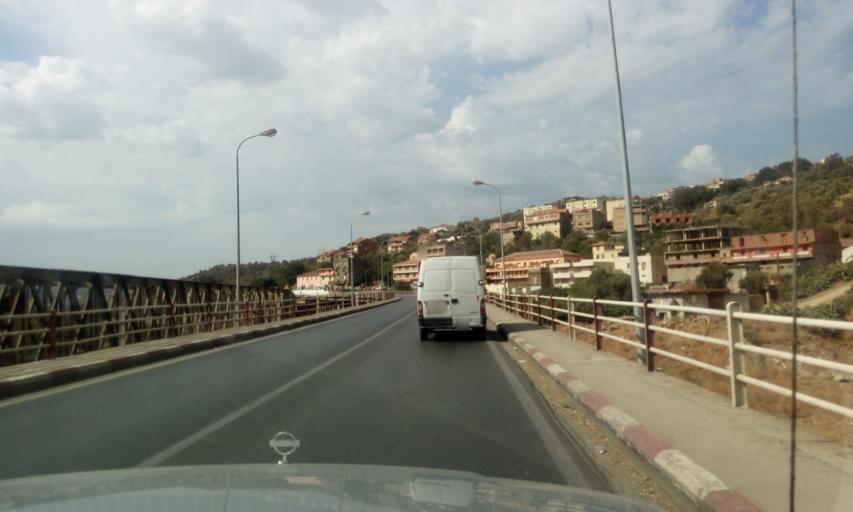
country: DZ
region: Bejaia
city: Seddouk
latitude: 36.6097
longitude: 4.6842
